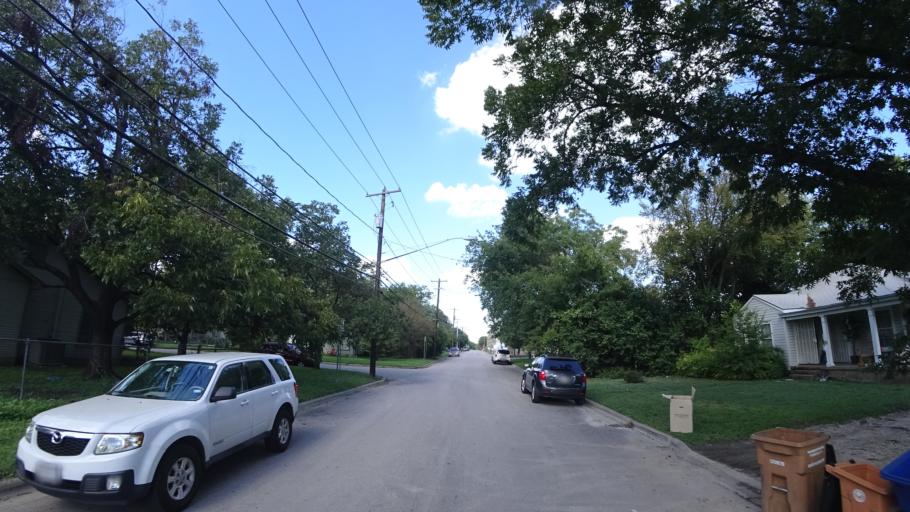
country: US
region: Texas
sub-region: Travis County
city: Austin
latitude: 30.3086
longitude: -97.7132
